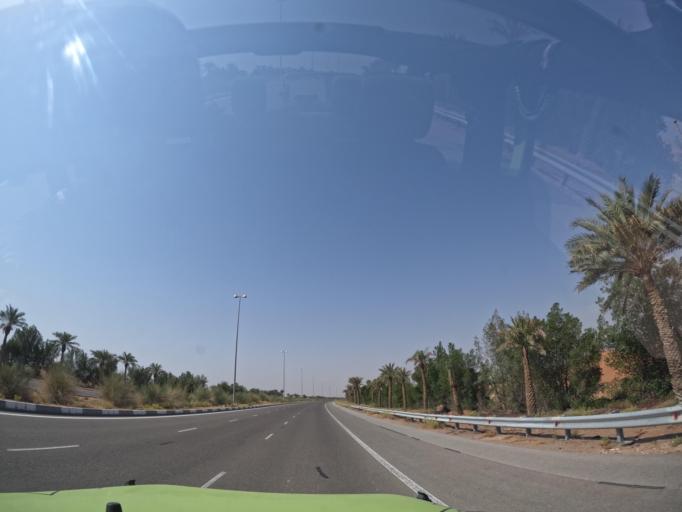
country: AE
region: Abu Dhabi
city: Al Ain
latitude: 24.2191
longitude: 55.6165
